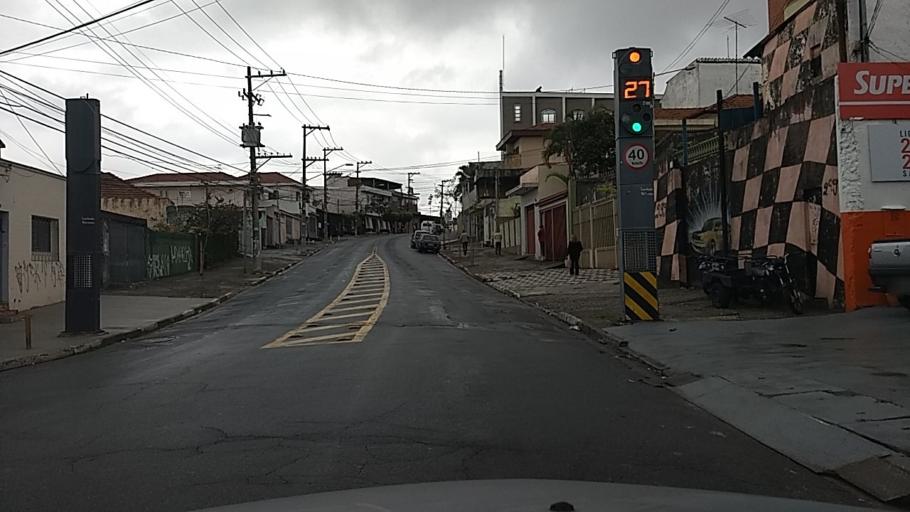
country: BR
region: Sao Paulo
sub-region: Guarulhos
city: Guarulhos
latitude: -23.4991
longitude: -46.5876
